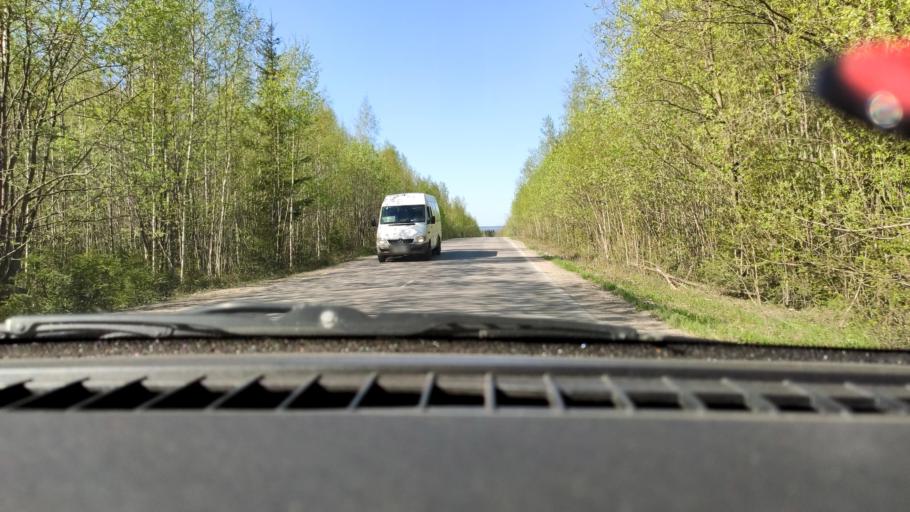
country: RU
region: Perm
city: Kondratovo
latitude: 58.0637
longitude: 56.0024
